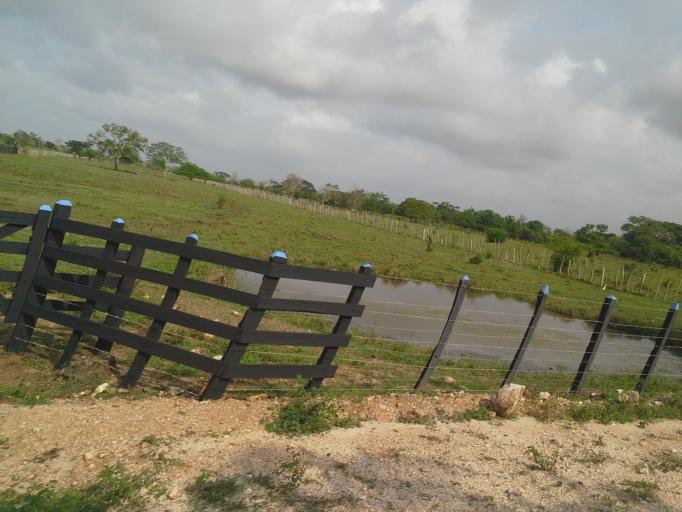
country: CO
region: Cordoba
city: Chima
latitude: 9.1886
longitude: -75.6054
